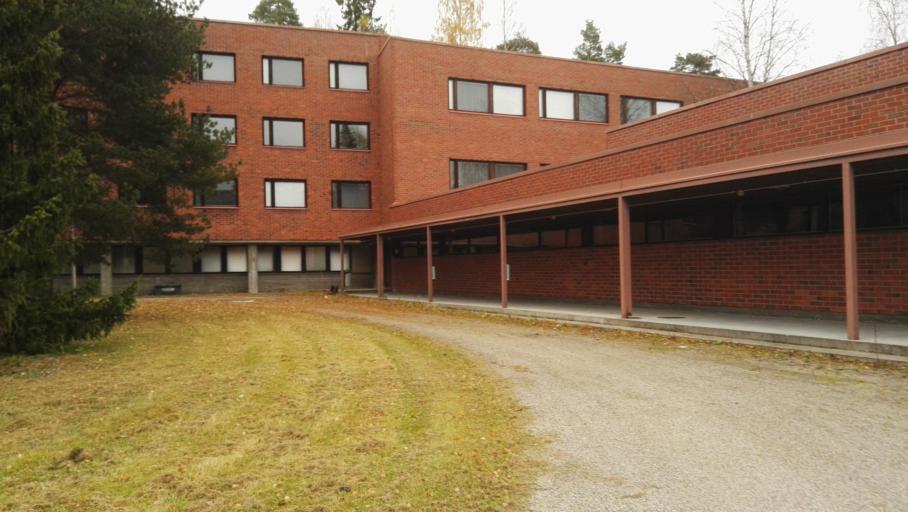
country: FI
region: Paijanne Tavastia
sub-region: Lahti
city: Lahti
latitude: 60.9665
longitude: 25.6203
